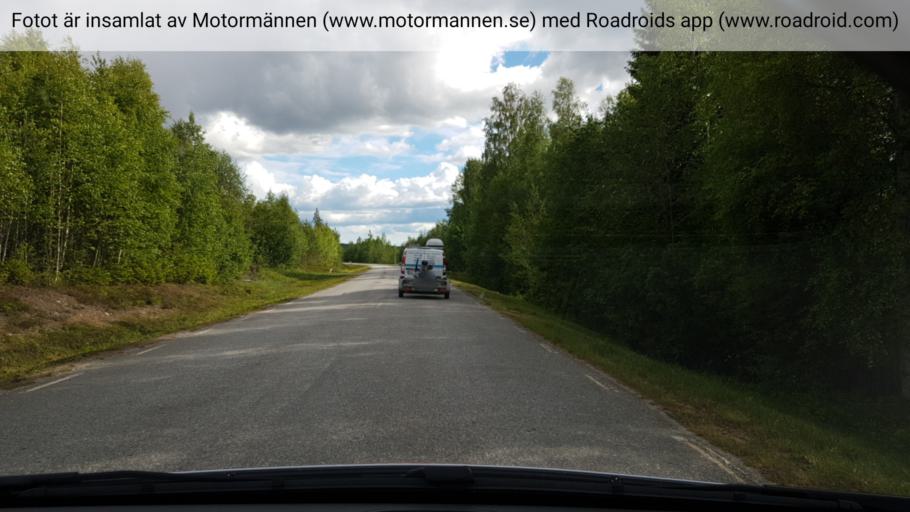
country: SE
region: Vaesterbotten
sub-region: Vannas Kommun
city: Vannasby
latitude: 64.0542
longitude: 19.9347
